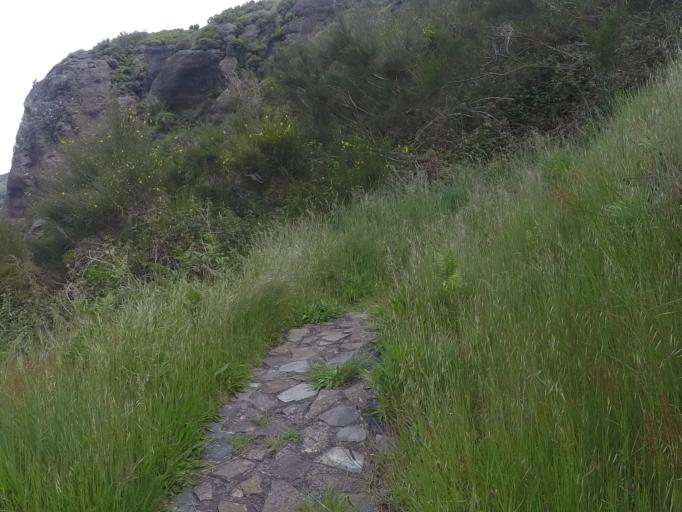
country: PT
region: Madeira
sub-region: Camara de Lobos
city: Curral das Freiras
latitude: 32.7404
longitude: -17.0052
